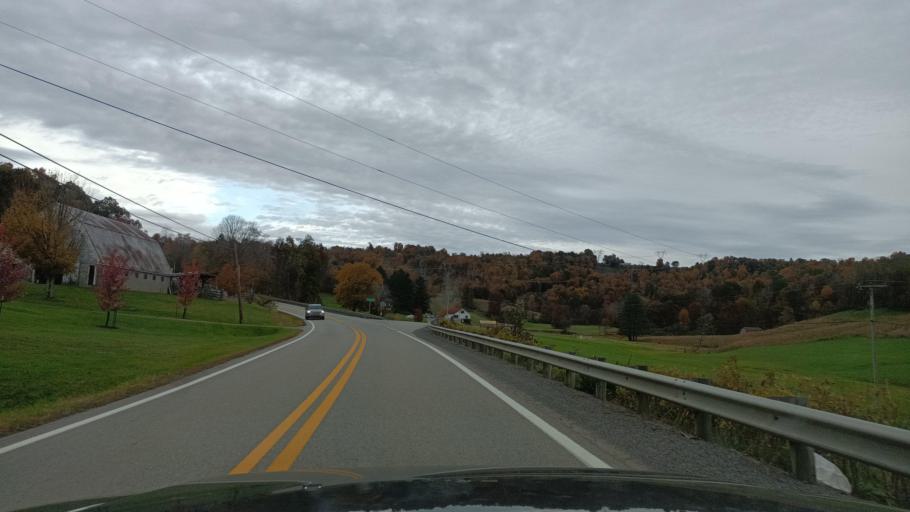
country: US
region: West Virginia
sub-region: Taylor County
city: Grafton
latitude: 39.3618
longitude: -79.9790
